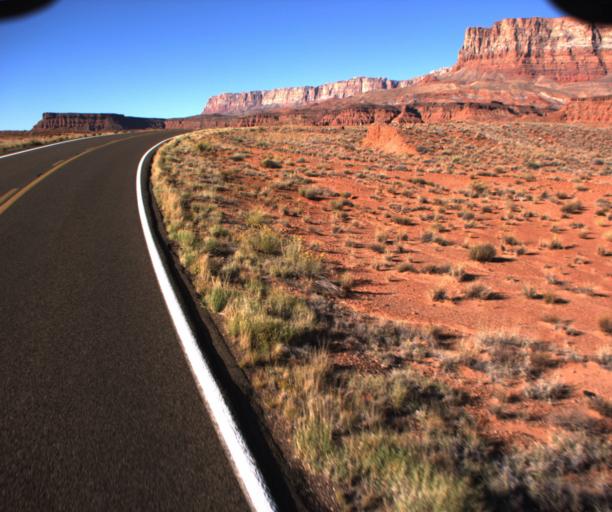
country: US
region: Arizona
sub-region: Coconino County
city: Page
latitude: 36.7808
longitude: -111.6895
